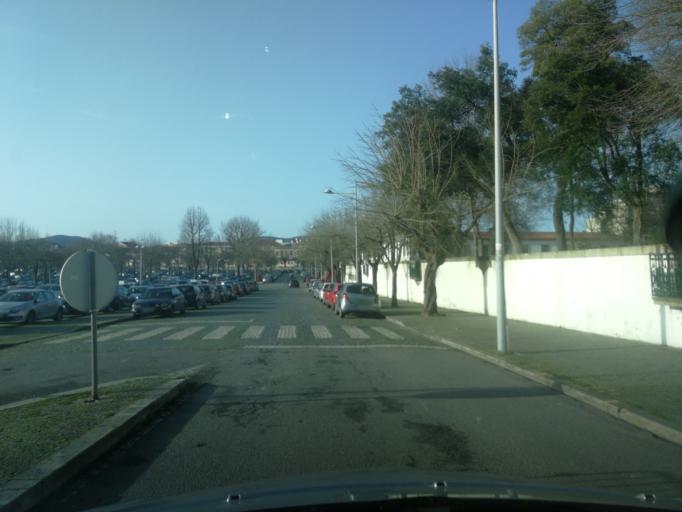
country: PT
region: Braga
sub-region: Barcelos
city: Barcelos
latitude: 41.5319
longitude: -8.6159
